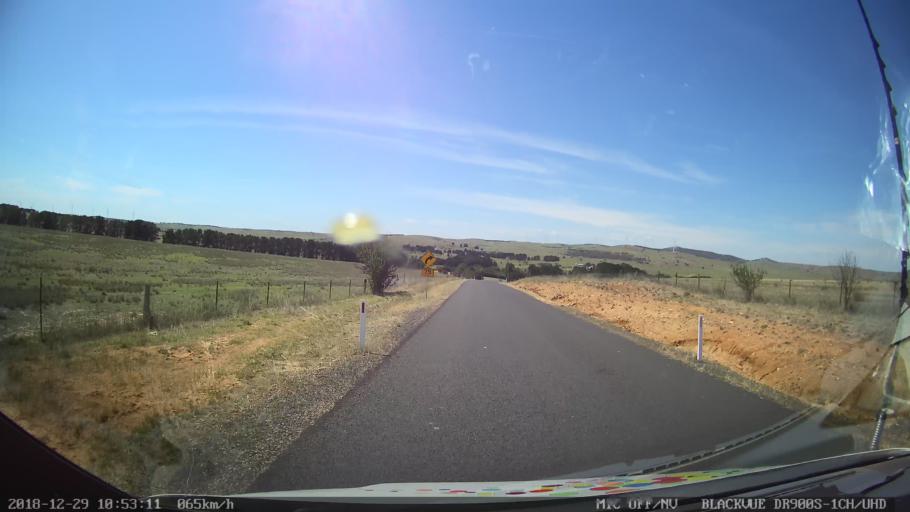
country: AU
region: New South Wales
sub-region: Palerang
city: Bungendore
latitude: -35.1062
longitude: 149.5213
